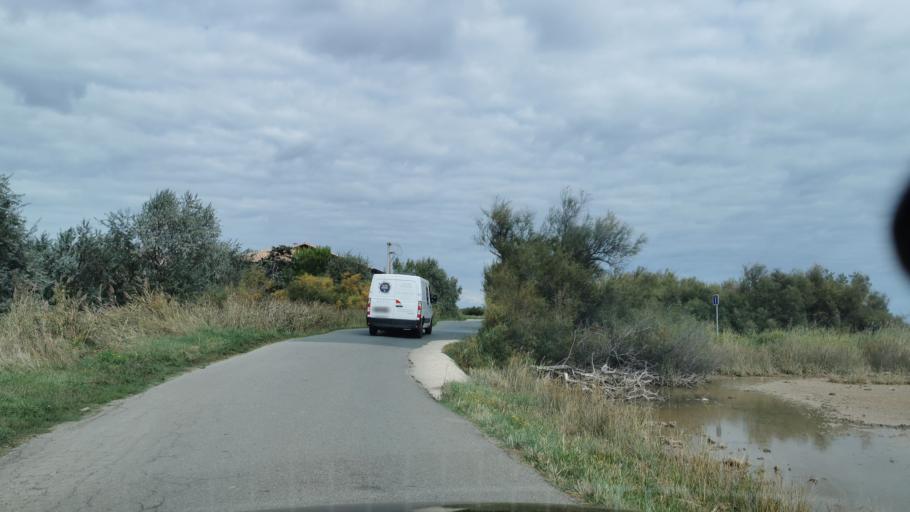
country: FR
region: Languedoc-Roussillon
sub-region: Departement de l'Aude
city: Fleury
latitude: 43.2076
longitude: 3.1940
